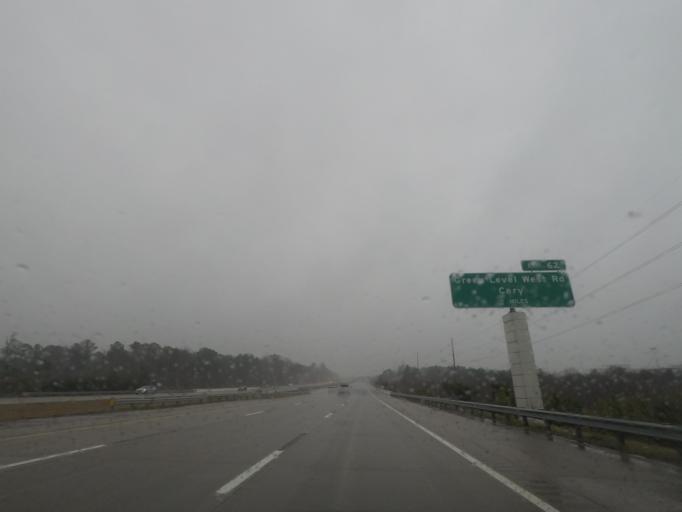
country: US
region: North Carolina
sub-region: Wake County
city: Green Level
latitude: 35.8163
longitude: -78.8925
